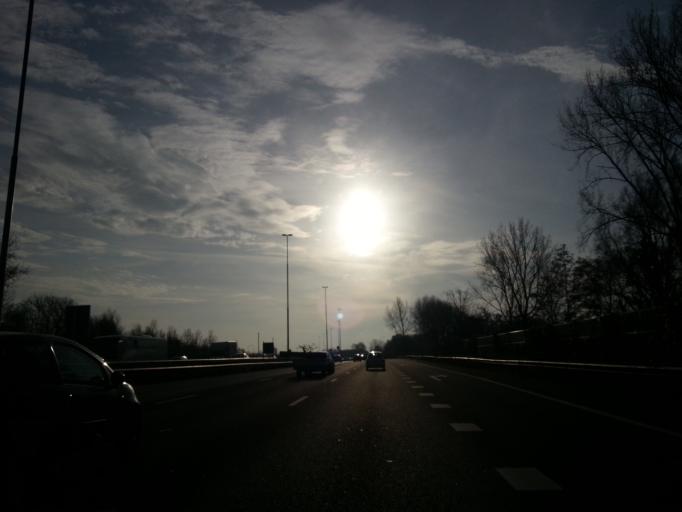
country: NL
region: South Holland
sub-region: Gemeente Schiedam
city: Schiedam
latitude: 51.9537
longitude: 4.4132
